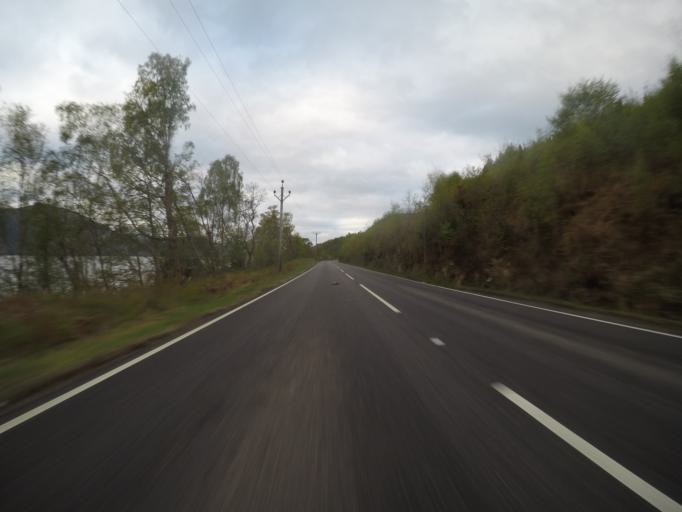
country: GB
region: Scotland
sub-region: Highland
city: Beauly
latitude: 57.1807
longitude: -4.6328
